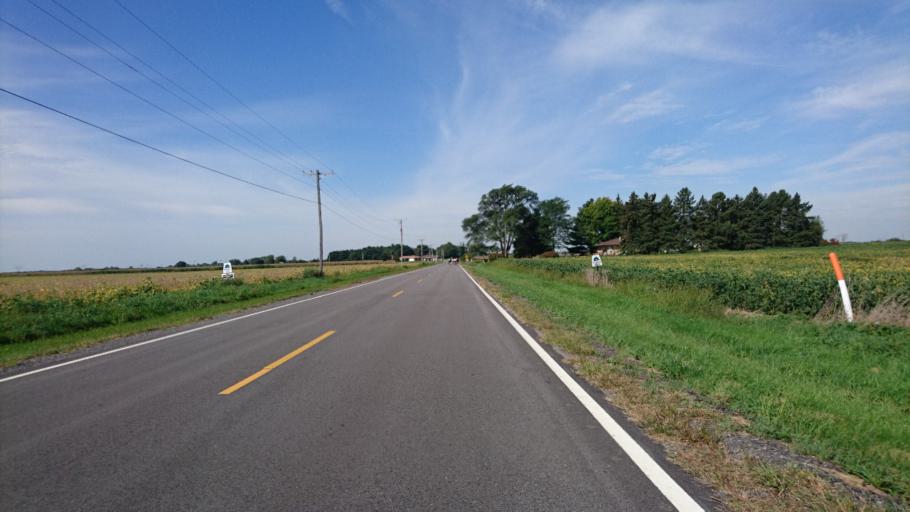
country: US
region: Illinois
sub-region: Will County
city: Elwood
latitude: 41.4082
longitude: -88.0878
